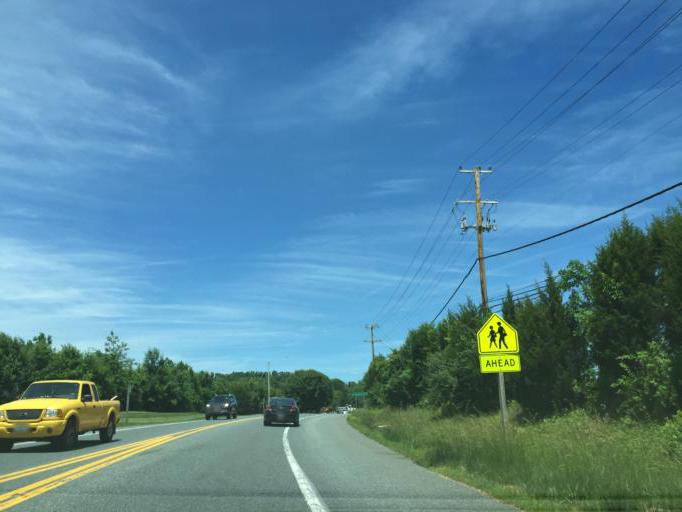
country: US
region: Maryland
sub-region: Harford County
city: South Bel Air
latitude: 39.5557
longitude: -76.3290
